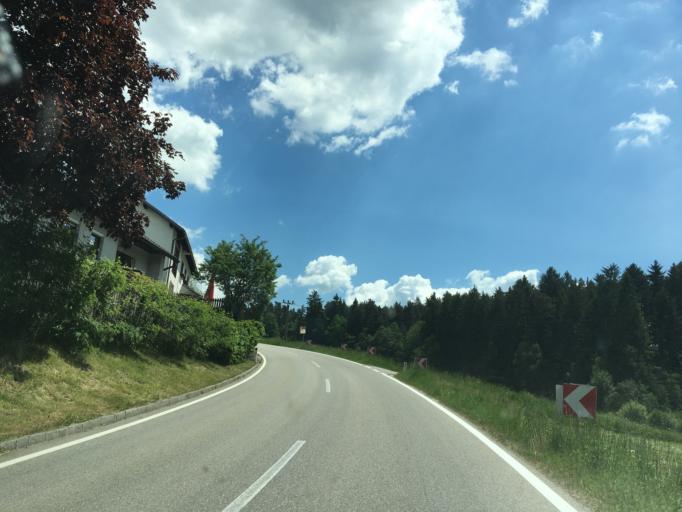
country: AT
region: Upper Austria
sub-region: Politischer Bezirk Freistadt
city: Freistadt
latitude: 48.4117
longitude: 14.5534
